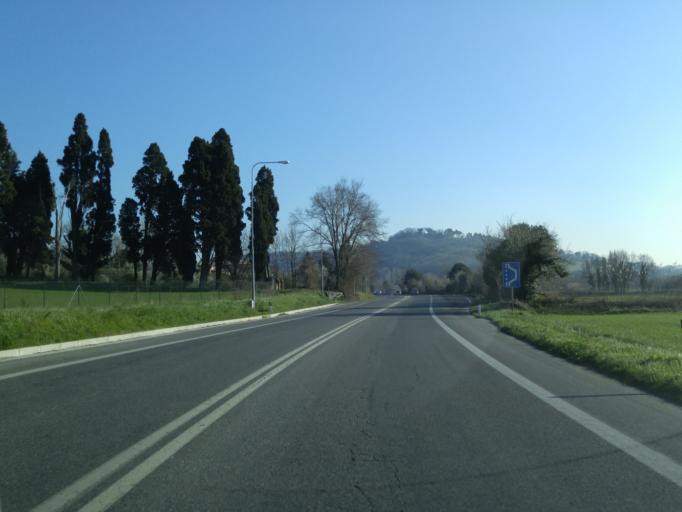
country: IT
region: The Marches
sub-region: Provincia di Pesaro e Urbino
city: Gradara
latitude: 43.9518
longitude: 12.7850
